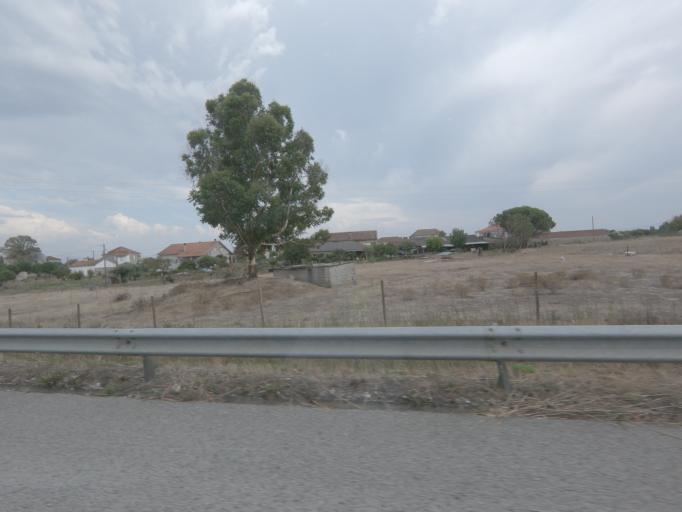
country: PT
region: Viseu
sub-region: Santa Comba Dao
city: Santa Comba Dao
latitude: 40.3749
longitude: -8.1245
